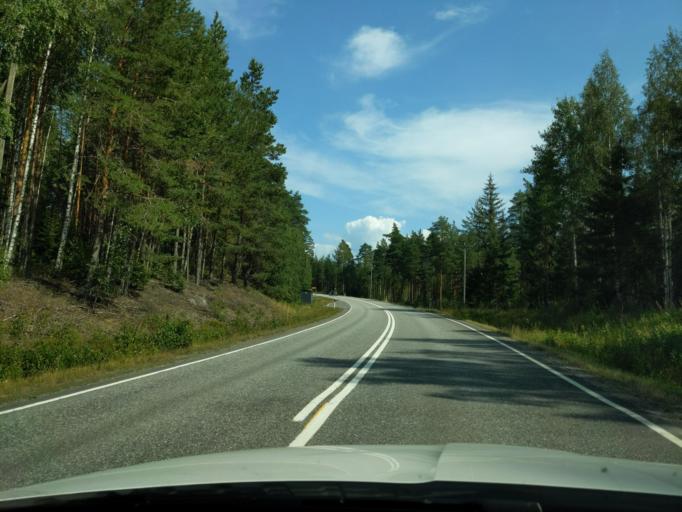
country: FI
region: Paijanne Tavastia
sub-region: Lahti
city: Padasjoki
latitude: 61.3271
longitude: 25.1916
